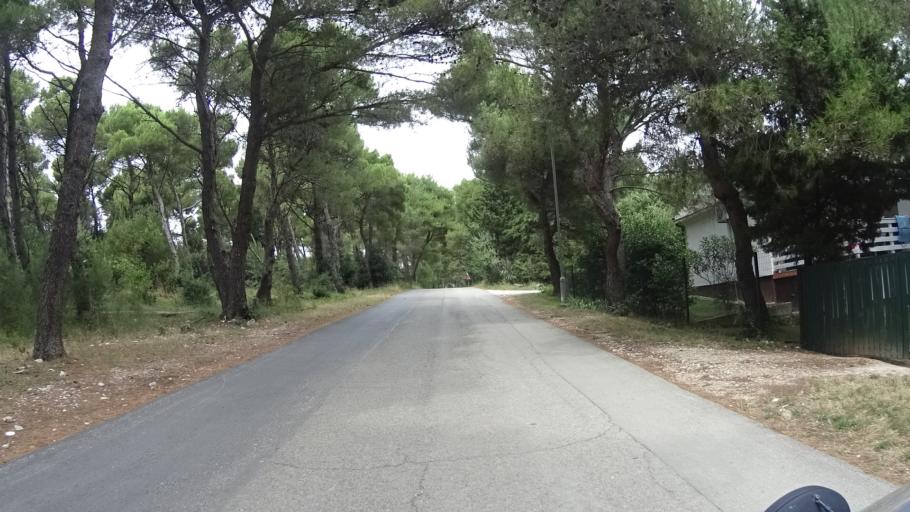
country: HR
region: Istarska
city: Medulin
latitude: 44.8036
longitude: 13.9069
